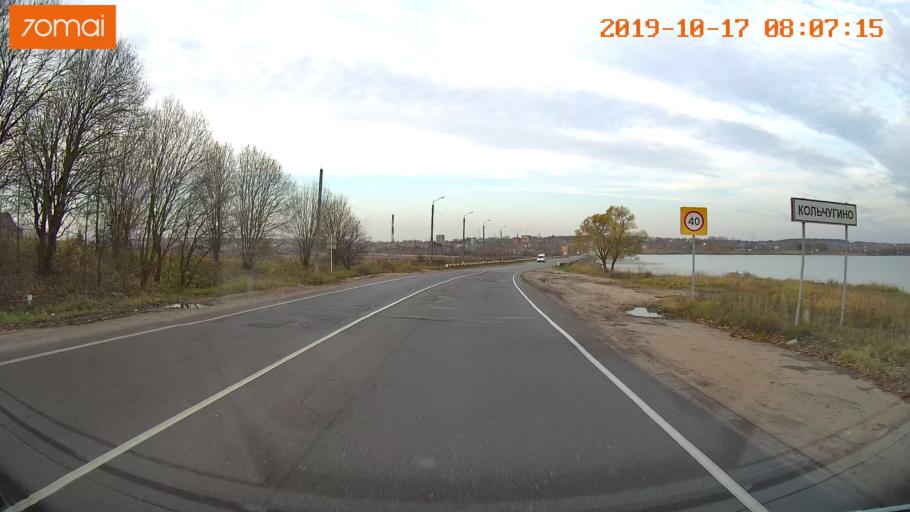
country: RU
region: Vladimir
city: Kol'chugino
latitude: 56.3162
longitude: 39.4023
